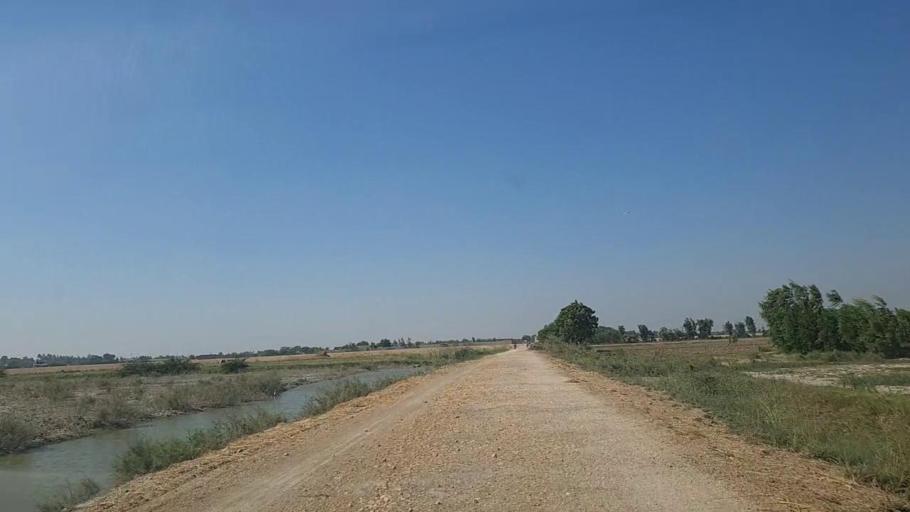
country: PK
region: Sindh
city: Thatta
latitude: 24.7687
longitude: 67.9462
